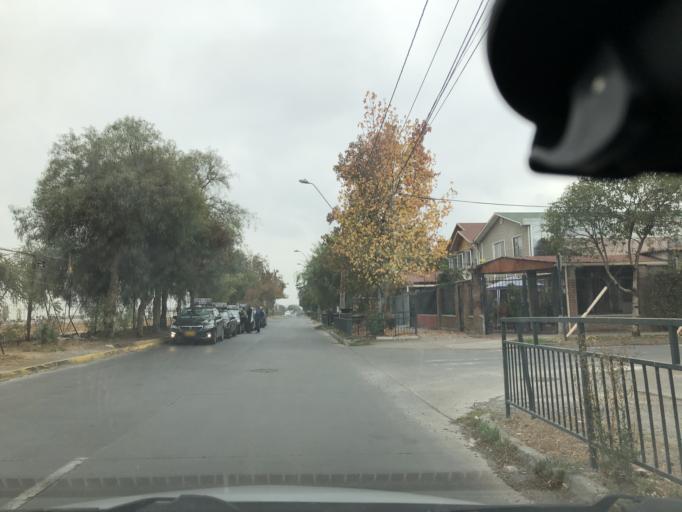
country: CL
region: Santiago Metropolitan
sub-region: Provincia de Santiago
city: La Pintana
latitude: -33.5746
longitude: -70.6105
